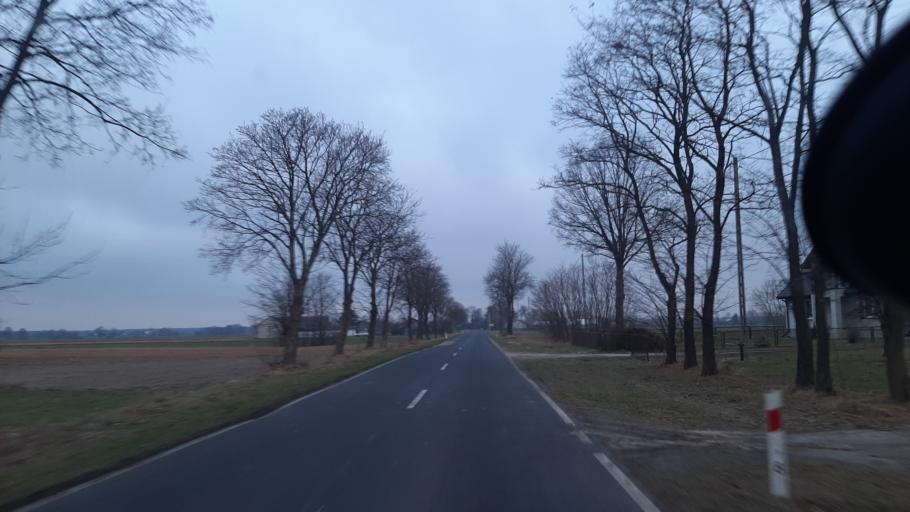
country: PL
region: Lublin Voivodeship
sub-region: Powiat parczewski
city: Debowa Kloda
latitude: 51.6349
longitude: 23.0670
